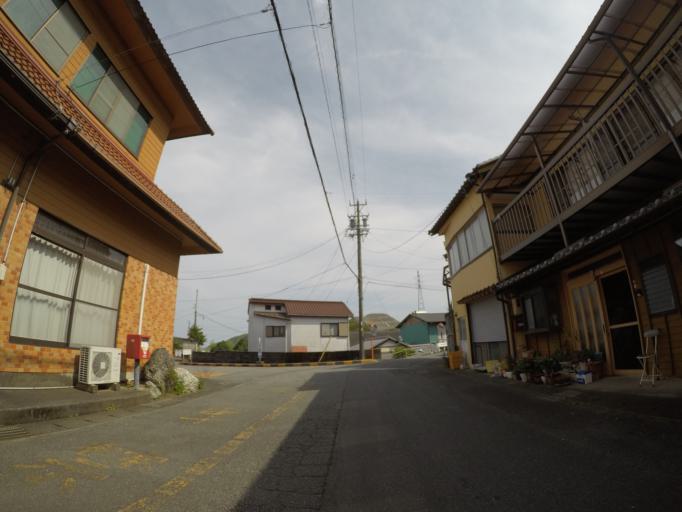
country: JP
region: Shizuoka
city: Shizuoka-shi
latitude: 35.0856
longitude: 138.4616
